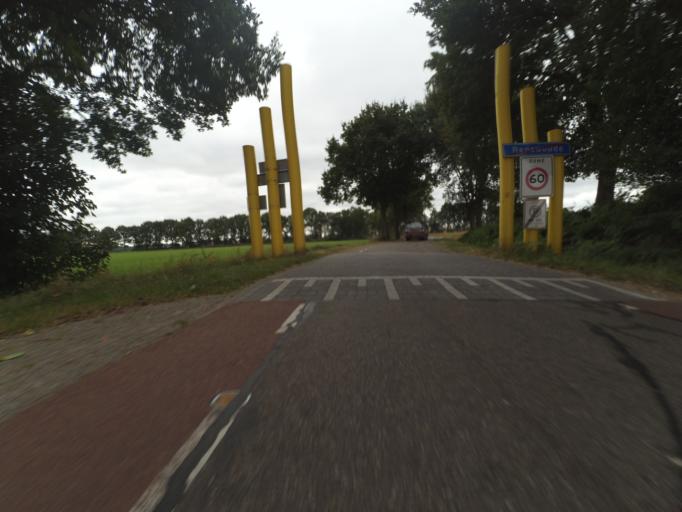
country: NL
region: Utrecht
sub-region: Gemeente Utrechtse Heuvelrug
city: Overberg
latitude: 52.0696
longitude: 5.5299
